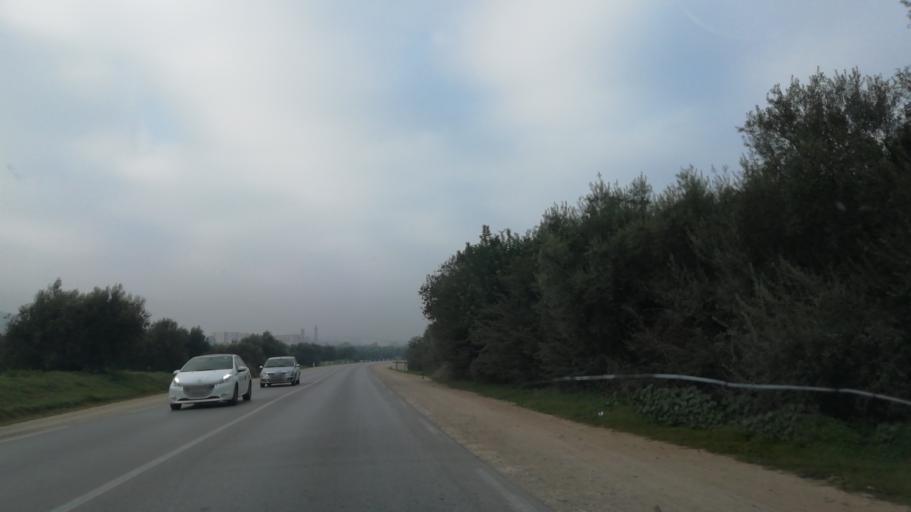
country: DZ
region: Relizane
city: Djidiouia
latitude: 35.9390
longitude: 0.8577
